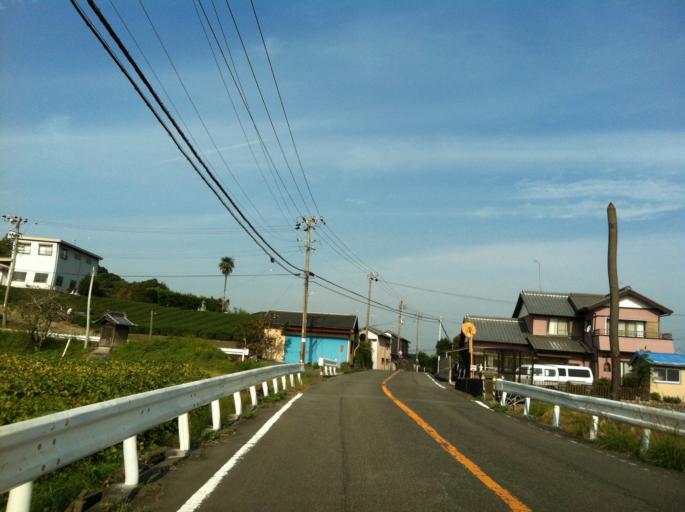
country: JP
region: Shizuoka
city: Sagara
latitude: 34.7509
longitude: 138.2024
